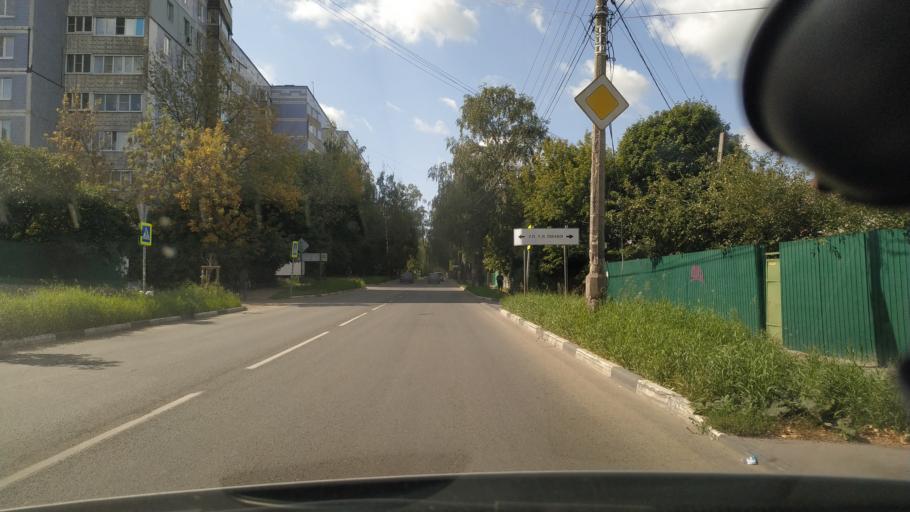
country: RU
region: Rjazan
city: Ryazan'
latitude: 54.6141
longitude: 39.7095
